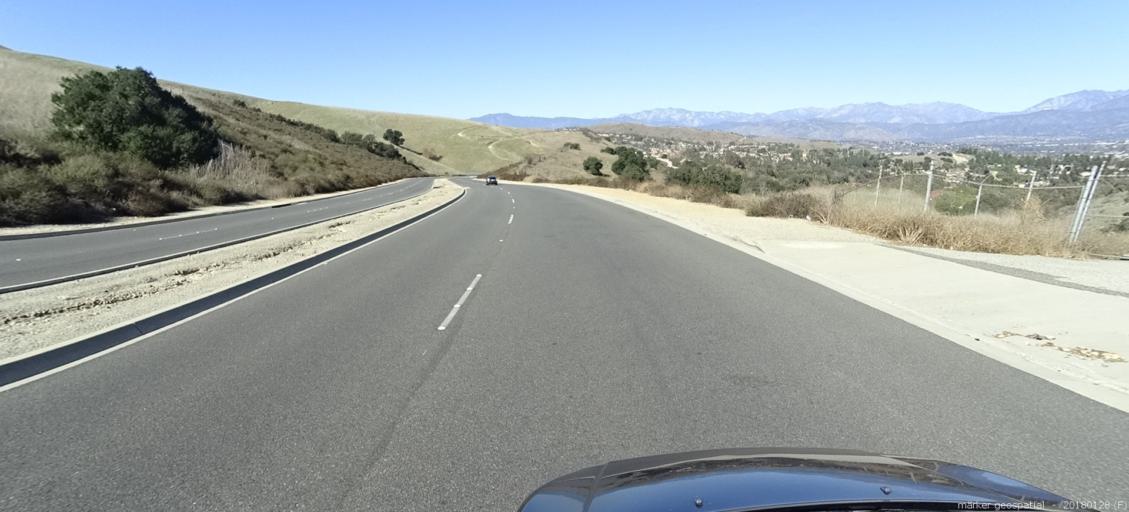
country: US
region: California
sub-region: San Bernardino County
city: Chino Hills
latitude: 34.0161
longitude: -117.7691
